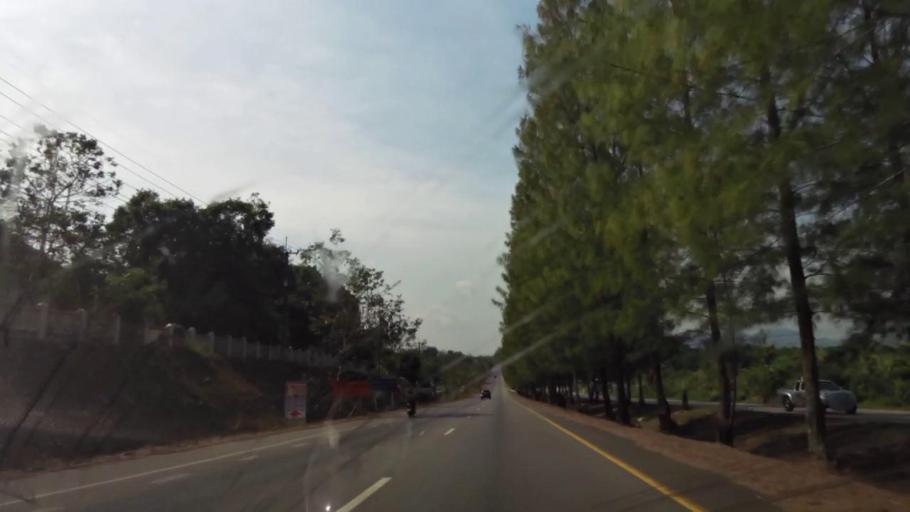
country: TH
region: Chanthaburi
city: Chanthaburi
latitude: 12.6657
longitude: 102.1027
